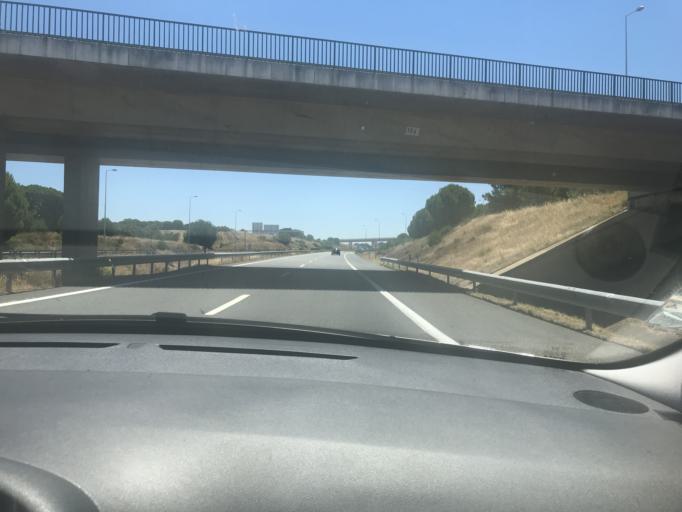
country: PT
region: Setubal
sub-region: Grandola
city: Grandola
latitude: 38.1240
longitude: -8.4139
